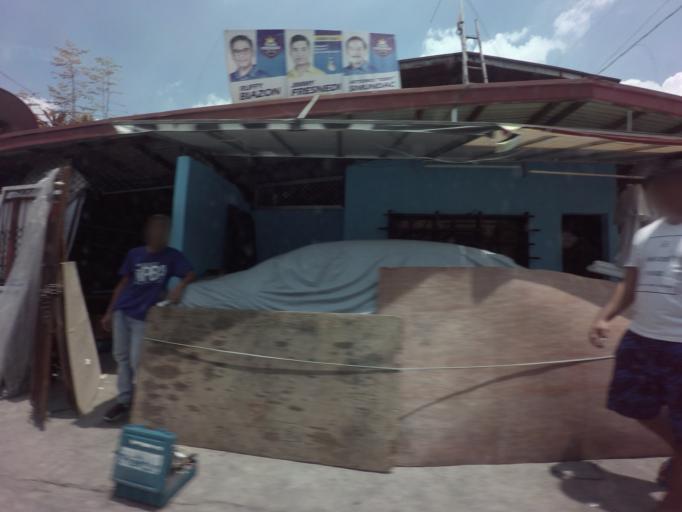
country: PH
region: Calabarzon
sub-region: Province of Laguna
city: San Pedro
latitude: 14.3872
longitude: 121.0501
